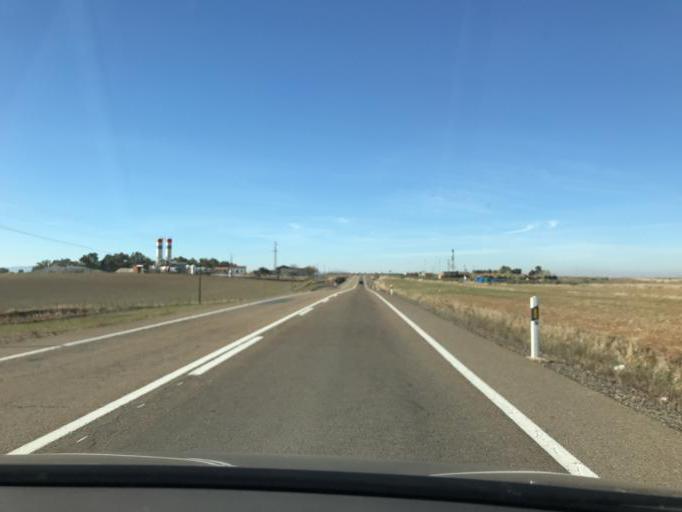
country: ES
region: Extremadura
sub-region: Provincia de Badajoz
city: Azuaga
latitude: 38.2600
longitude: -5.7070
